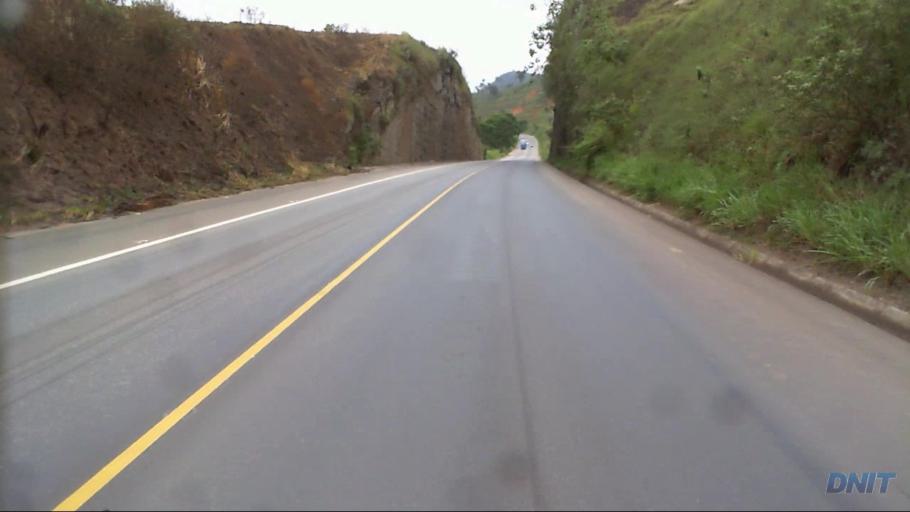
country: BR
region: Minas Gerais
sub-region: Coronel Fabriciano
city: Coronel Fabriciano
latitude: -19.5255
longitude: -42.6625
